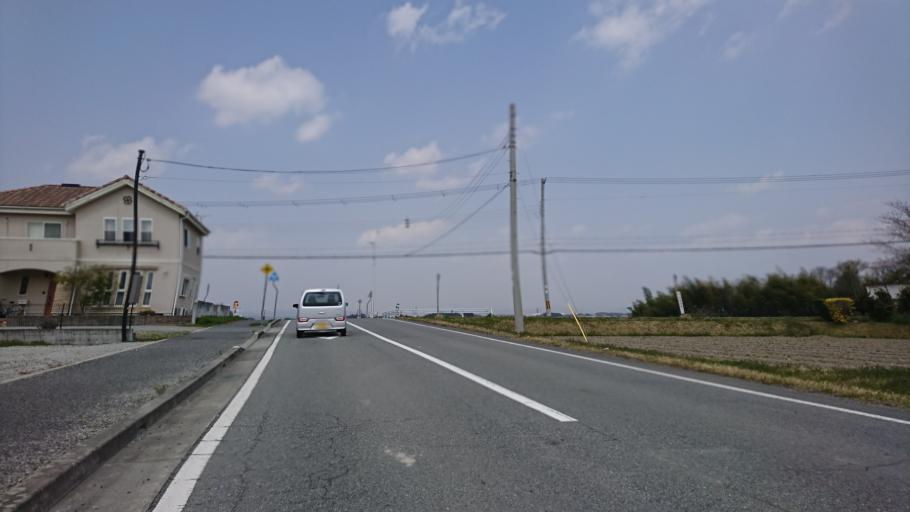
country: JP
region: Hyogo
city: Ono
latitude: 34.8366
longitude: 134.9103
